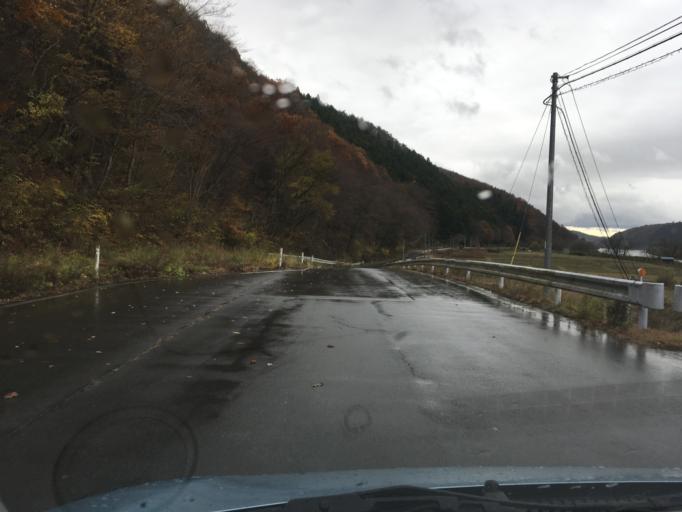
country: JP
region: Iwate
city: Ichinoseki
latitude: 38.8227
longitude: 141.2550
